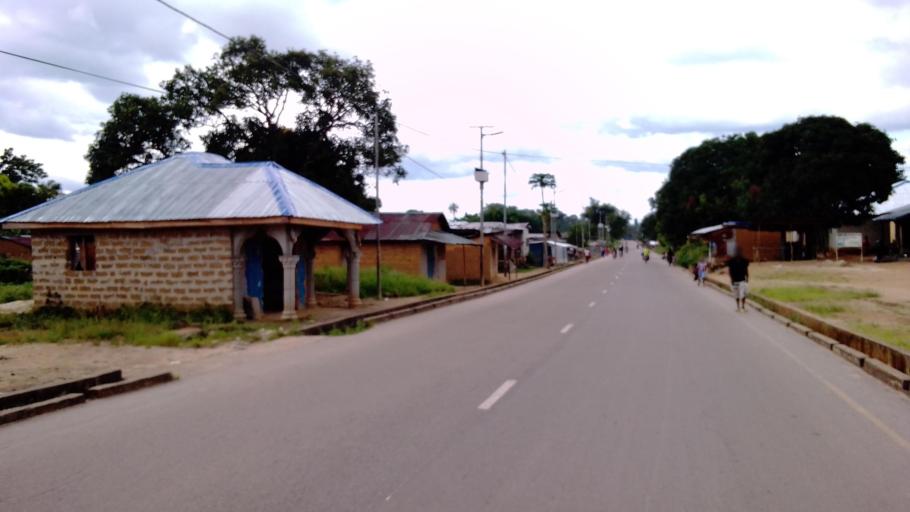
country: SL
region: Eastern Province
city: Koidu
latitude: 8.6523
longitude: -10.9753
